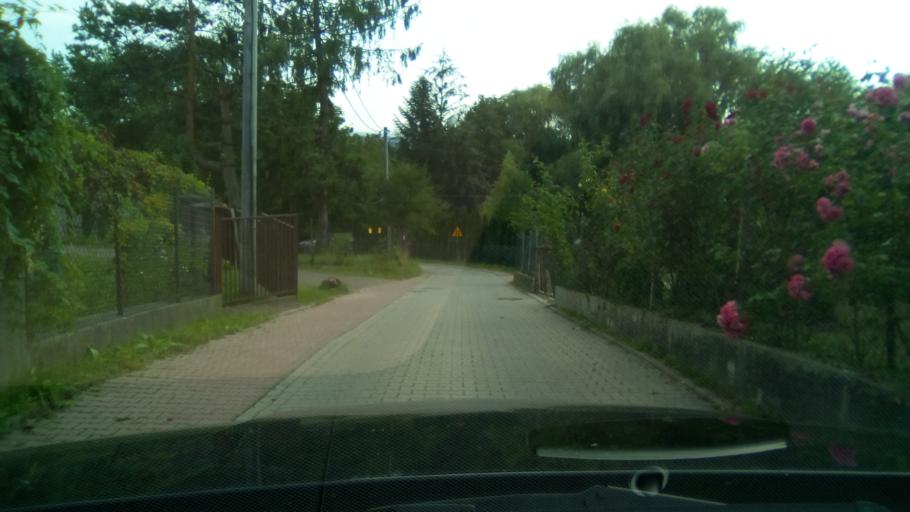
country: PL
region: Lesser Poland Voivodeship
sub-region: Krakow
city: Krakow
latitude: 50.0493
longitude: 19.8950
